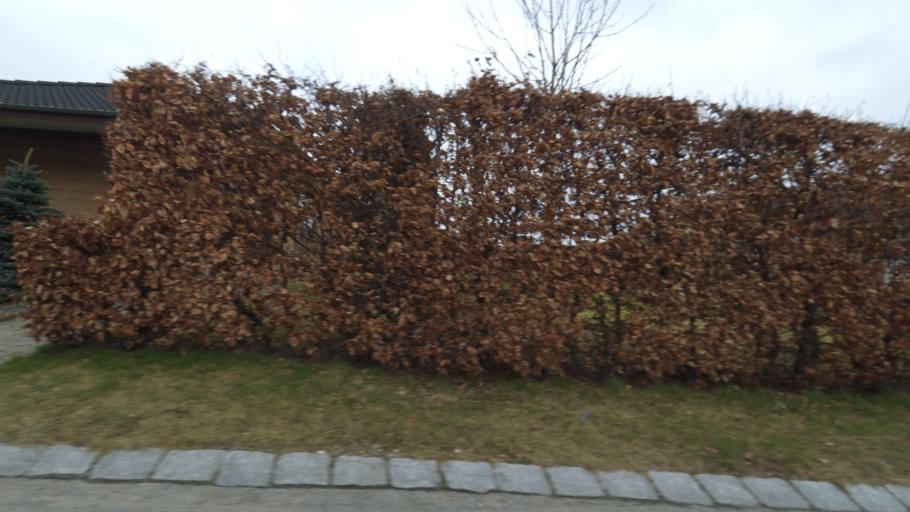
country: DK
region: Central Jutland
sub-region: Arhus Kommune
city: Tranbjerg
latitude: 56.0960
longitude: 10.1075
